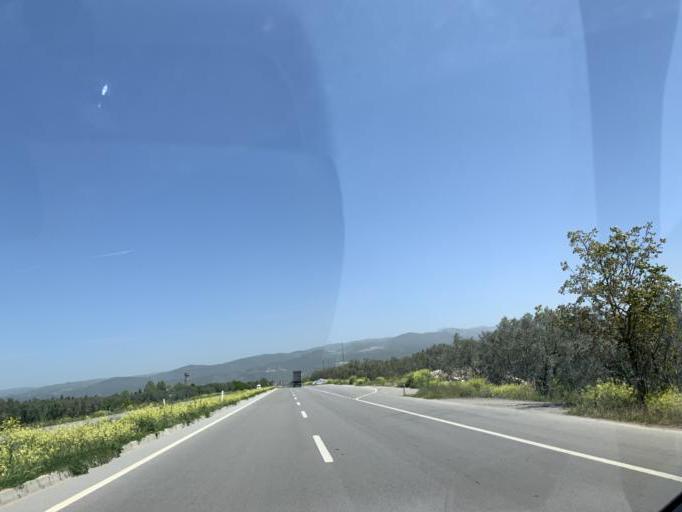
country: TR
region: Bursa
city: Iznik
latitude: 40.4009
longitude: 29.6973
